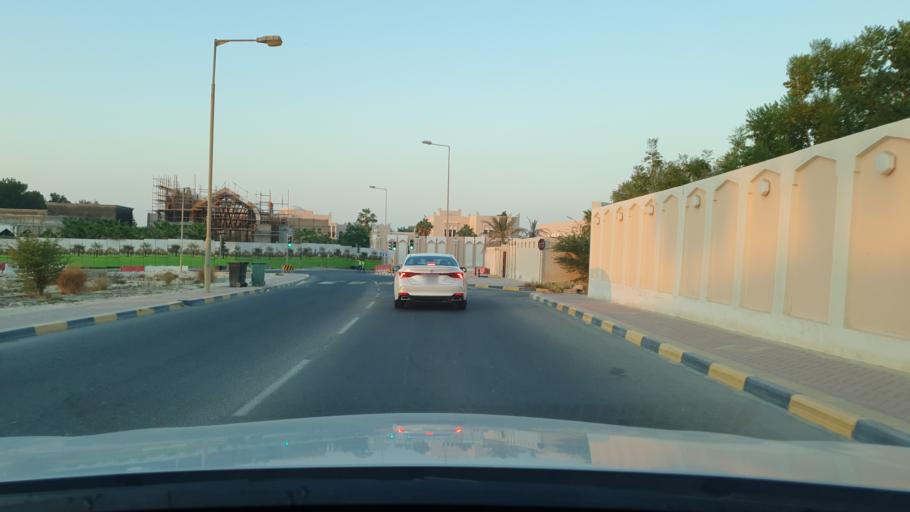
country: BH
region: Northern
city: Ar Rifa'
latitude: 26.1397
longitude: 50.5328
